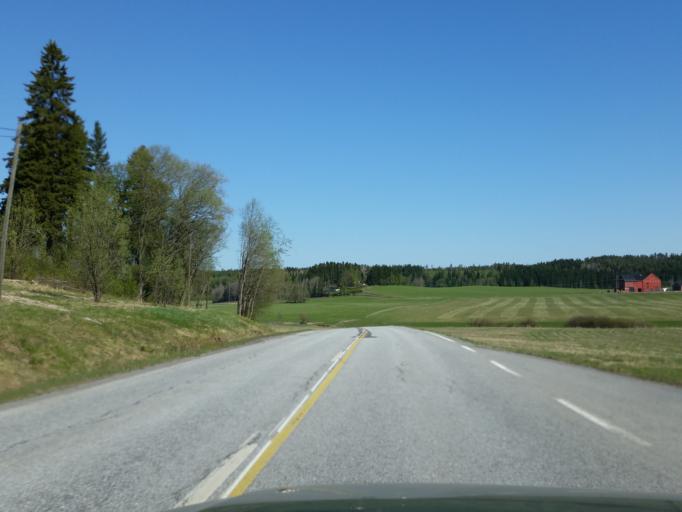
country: FI
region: Uusimaa
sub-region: Helsinki
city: Siuntio
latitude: 60.1721
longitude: 24.1628
